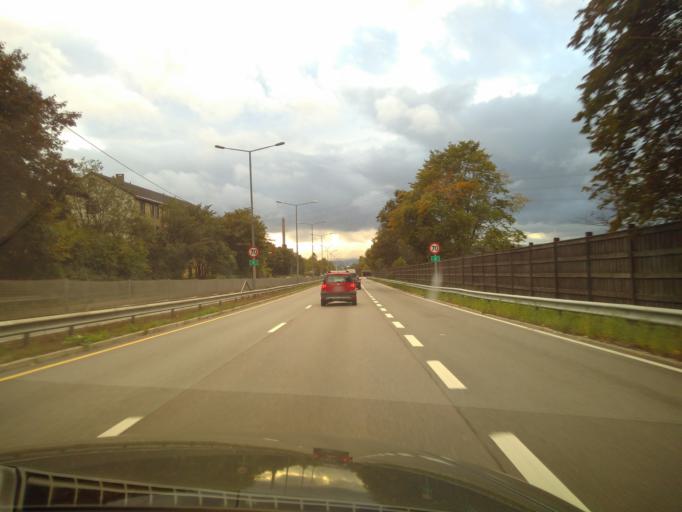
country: NO
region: Oslo
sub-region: Oslo
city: Oslo
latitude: 59.9418
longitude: 10.8026
